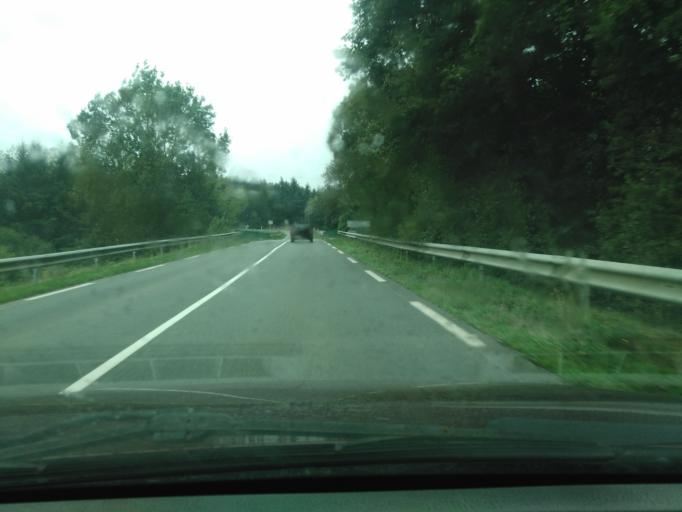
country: FR
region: Pays de la Loire
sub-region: Departement de la Vendee
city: Sainte-Hermine
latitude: 46.5880
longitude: -1.1166
